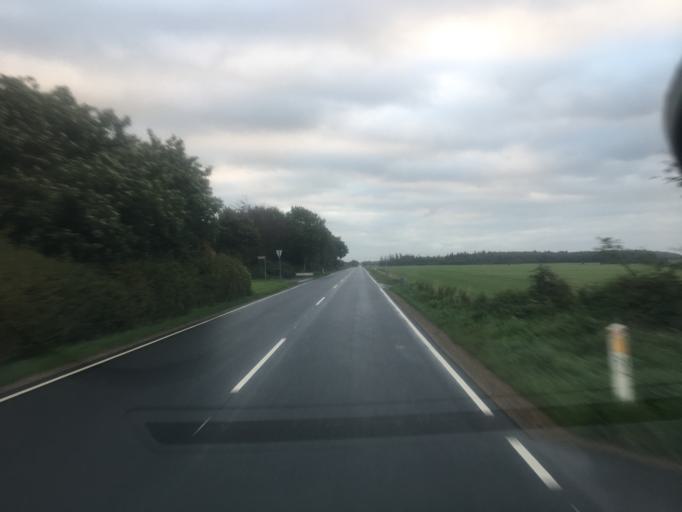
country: DK
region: South Denmark
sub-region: Tonder Kommune
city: Logumkloster
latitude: 54.9979
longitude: 8.9295
